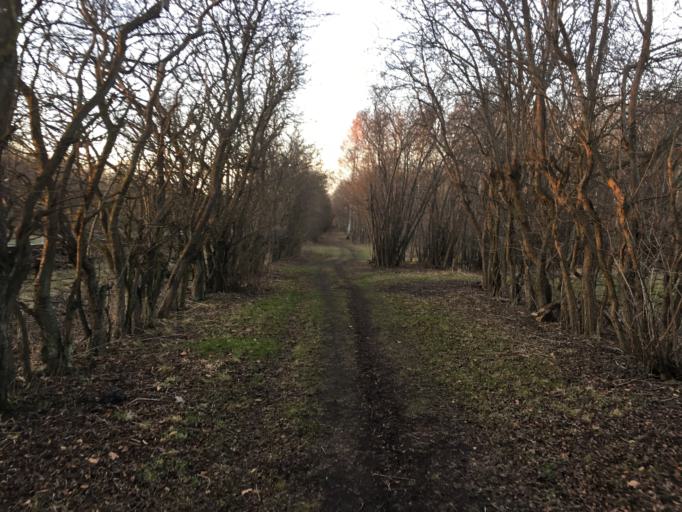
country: SE
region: Skane
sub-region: Burlovs Kommun
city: Arloev
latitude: 55.6516
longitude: 13.0742
